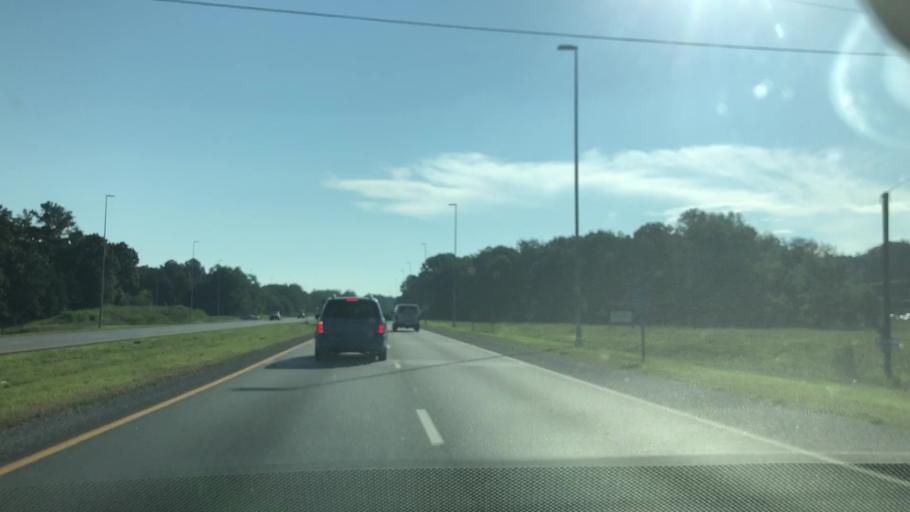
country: US
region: Alabama
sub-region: Calhoun County
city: West End-Cobb Town
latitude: 33.6358
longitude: -85.9080
